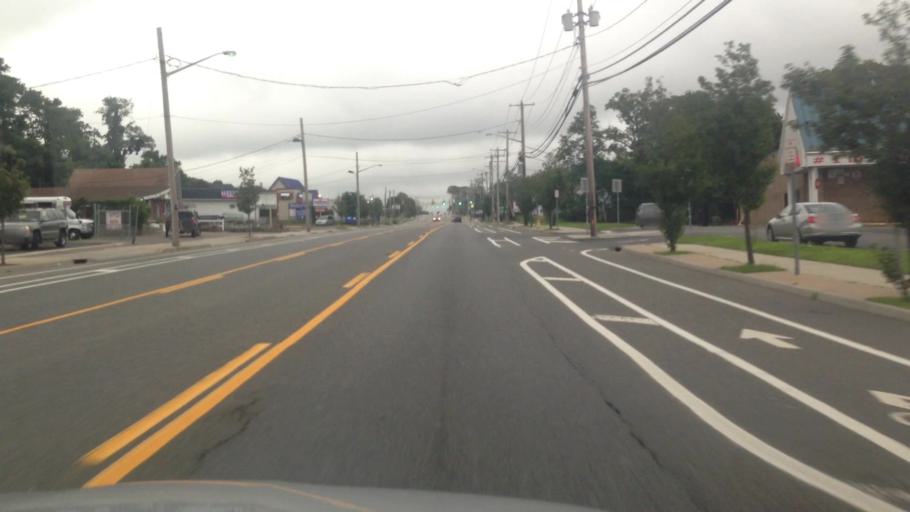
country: US
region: New York
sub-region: Suffolk County
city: Ronkonkoma
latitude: 40.8276
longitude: -73.1011
